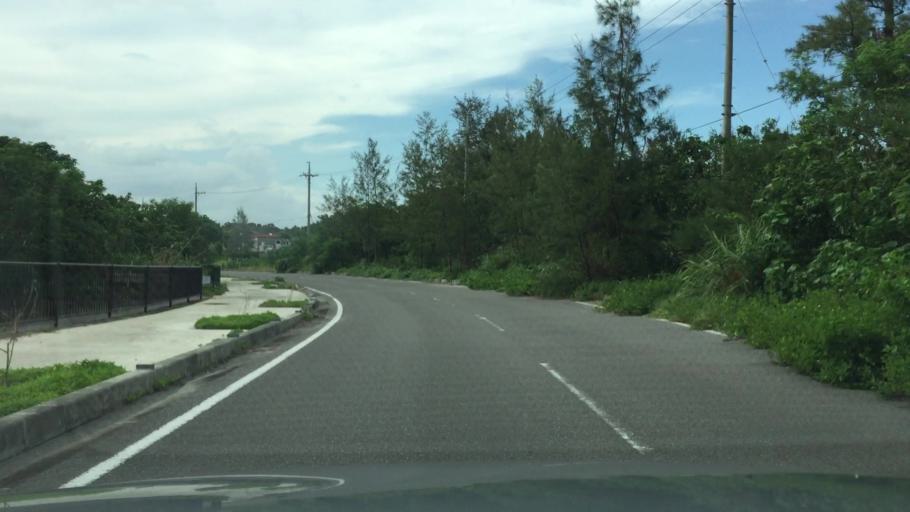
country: JP
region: Okinawa
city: Ishigaki
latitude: 24.4654
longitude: 124.1420
